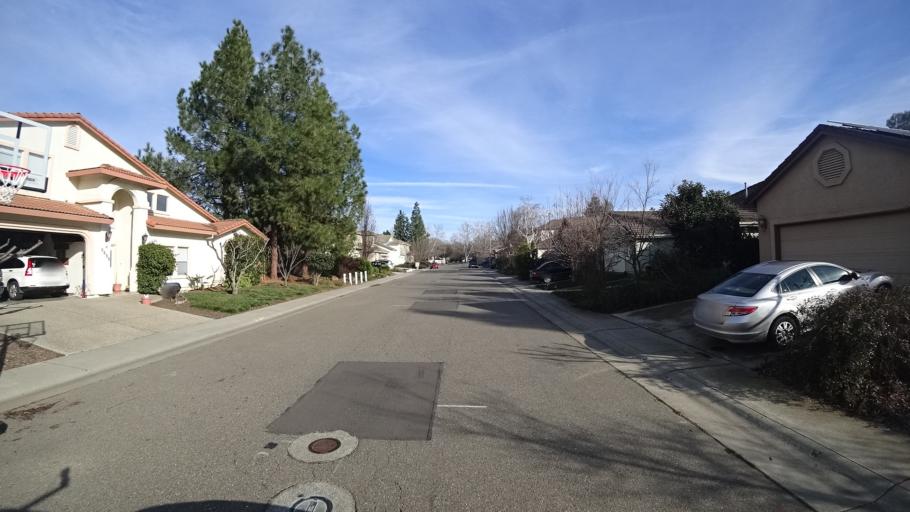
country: US
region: California
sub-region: Yolo County
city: Davis
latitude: 38.5464
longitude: -121.7083
